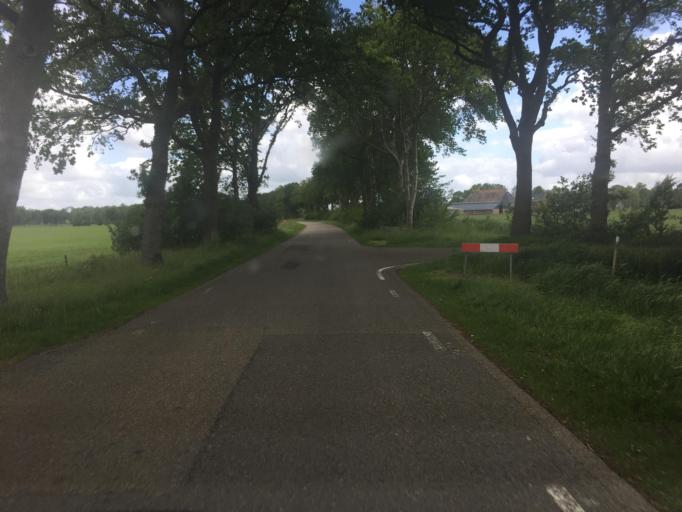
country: NL
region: Friesland
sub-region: Gemeente Heerenveen
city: Oudeschoot
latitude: 52.9215
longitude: 5.9229
